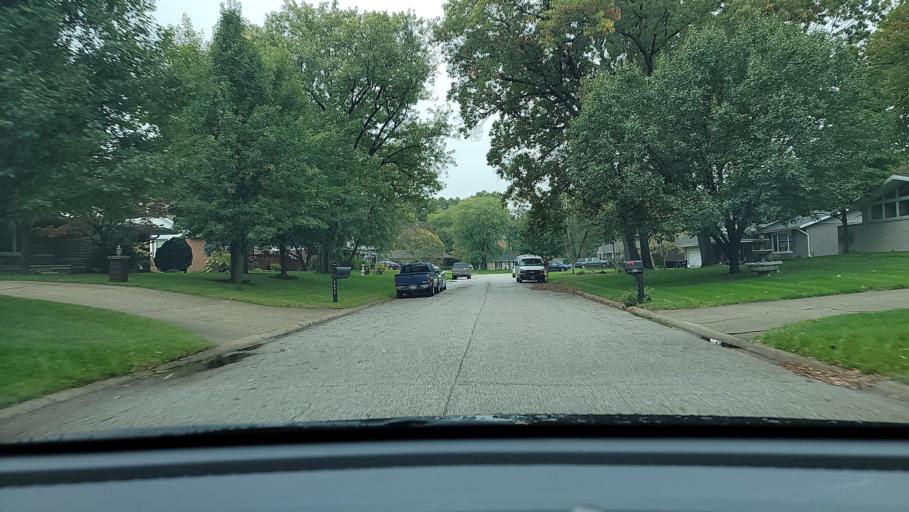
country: US
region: Indiana
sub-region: Porter County
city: Portage
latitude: 41.5739
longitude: -87.1788
